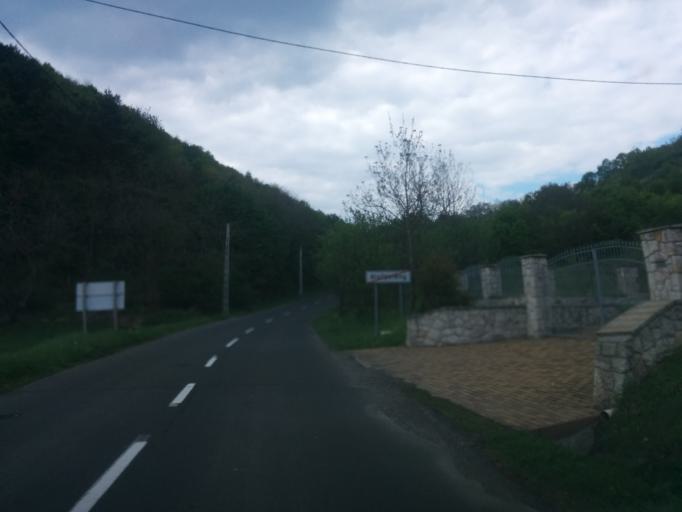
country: HU
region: Nograd
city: Romhany
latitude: 47.8812
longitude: 19.2362
